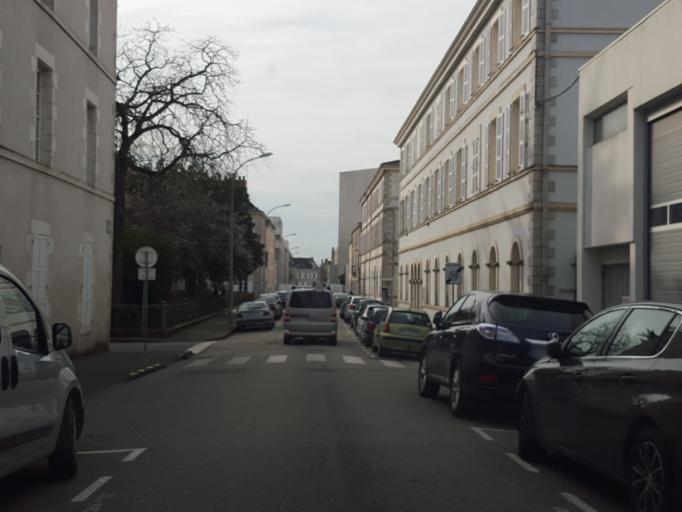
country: FR
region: Pays de la Loire
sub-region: Departement de la Vendee
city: La Roche-sur-Yon
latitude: 46.6688
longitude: -1.4275
